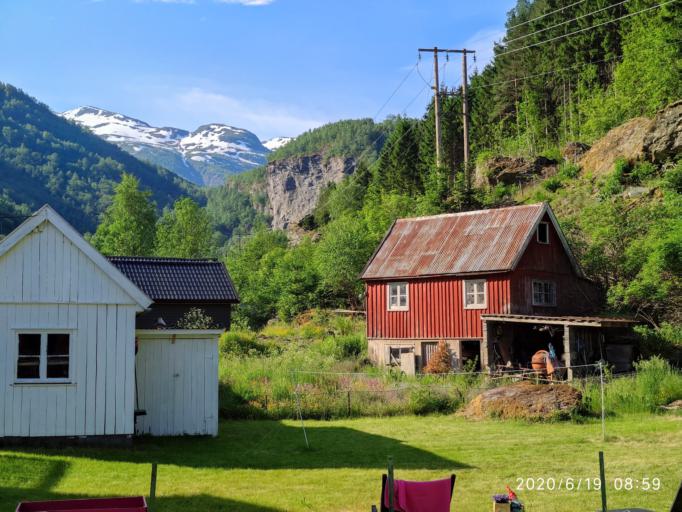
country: NO
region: Sogn og Fjordane
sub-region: Aurland
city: Aurlandsvangen
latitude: 60.8368
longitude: 7.1189
